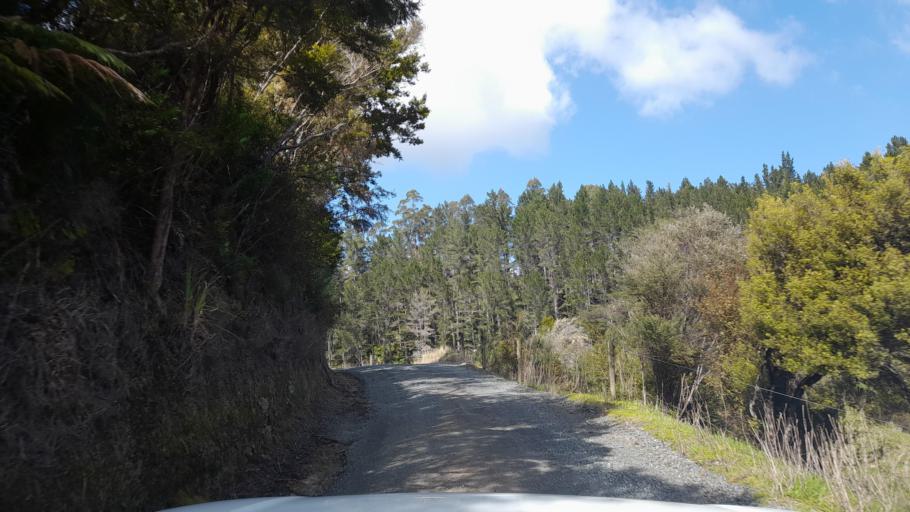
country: NZ
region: Northland
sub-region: Far North District
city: Waimate North
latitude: -35.1590
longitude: 173.7123
